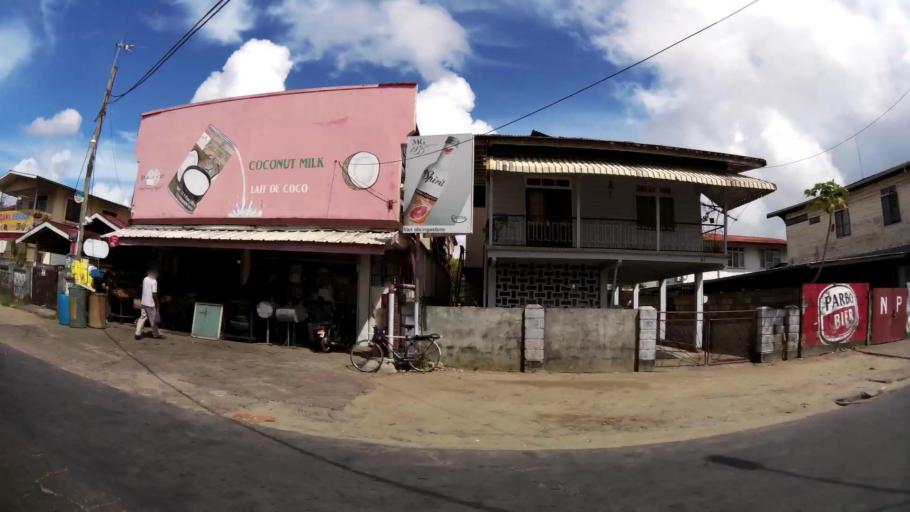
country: SR
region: Paramaribo
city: Paramaribo
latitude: 5.8285
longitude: -55.1752
